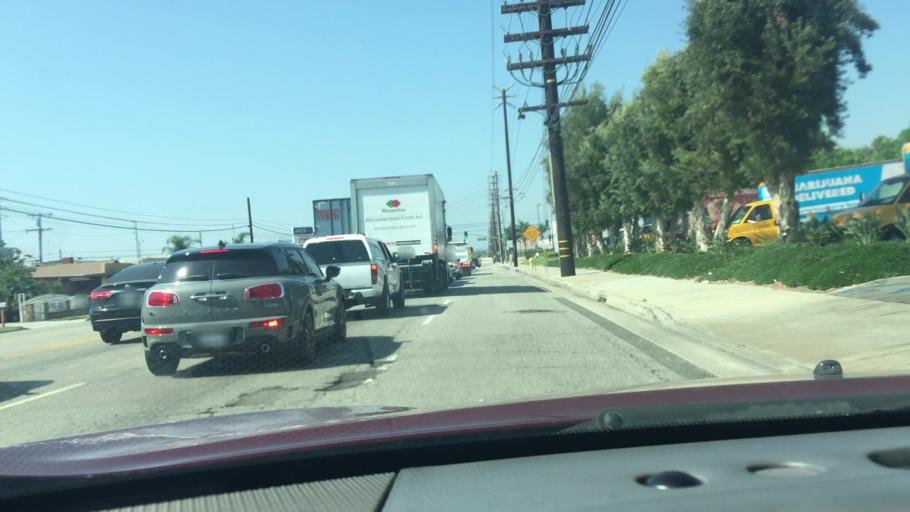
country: US
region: California
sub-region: Los Angeles County
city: Norwalk
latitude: 33.9011
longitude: -118.0465
